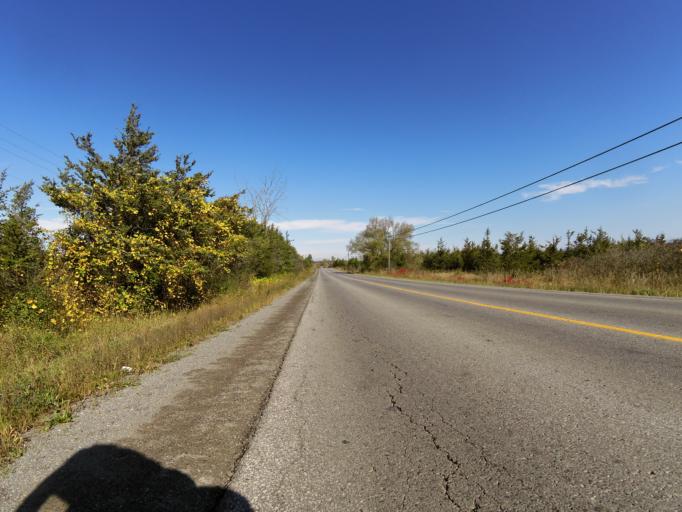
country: CA
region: Ontario
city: Prince Edward
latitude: 44.0178
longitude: -77.3647
